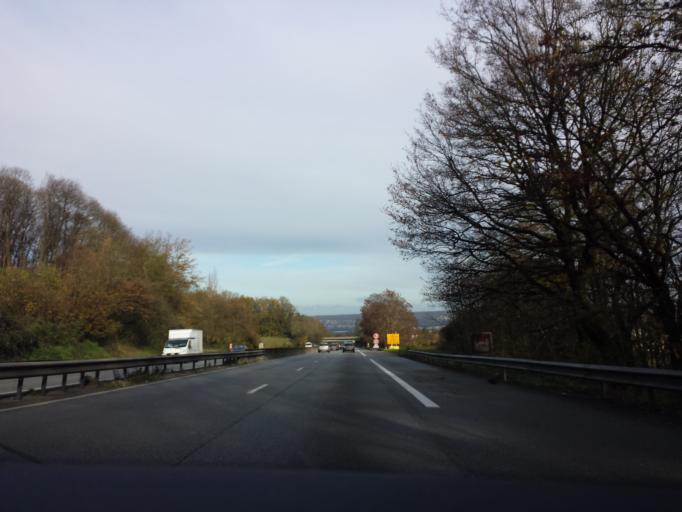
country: FR
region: Ile-de-France
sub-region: Departement des Yvelines
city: Orgeval
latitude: 48.9064
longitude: 2.0054
